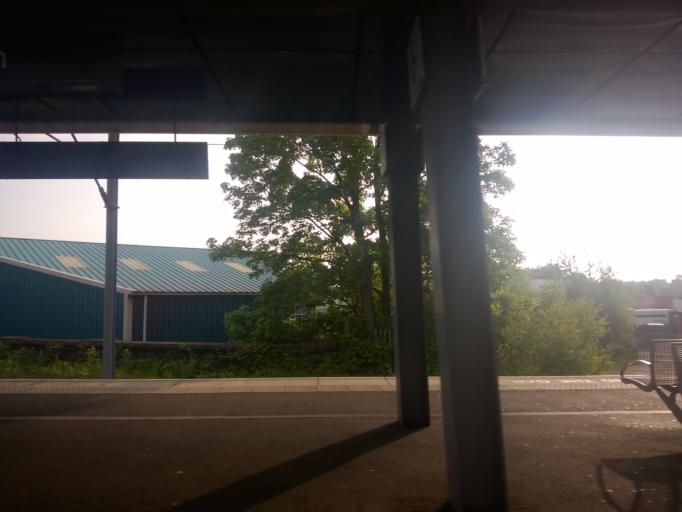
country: GB
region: England
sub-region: Warwickshire
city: Nuneaton
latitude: 52.5268
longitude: -1.4639
